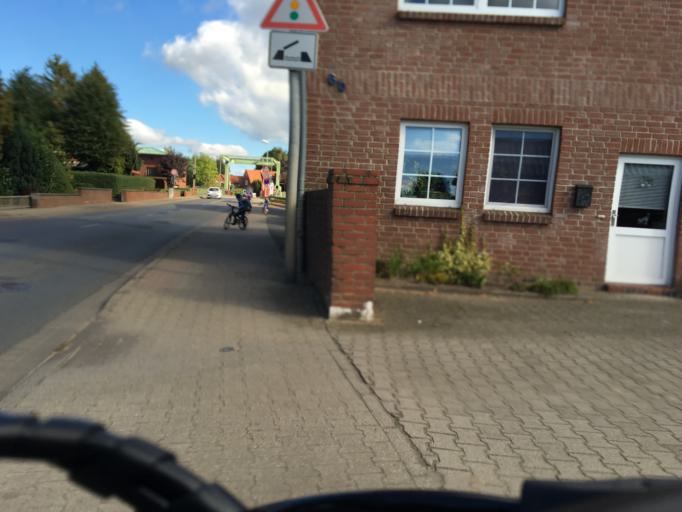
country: DE
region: Lower Saxony
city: Bardowick
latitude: 53.3000
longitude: 10.3962
